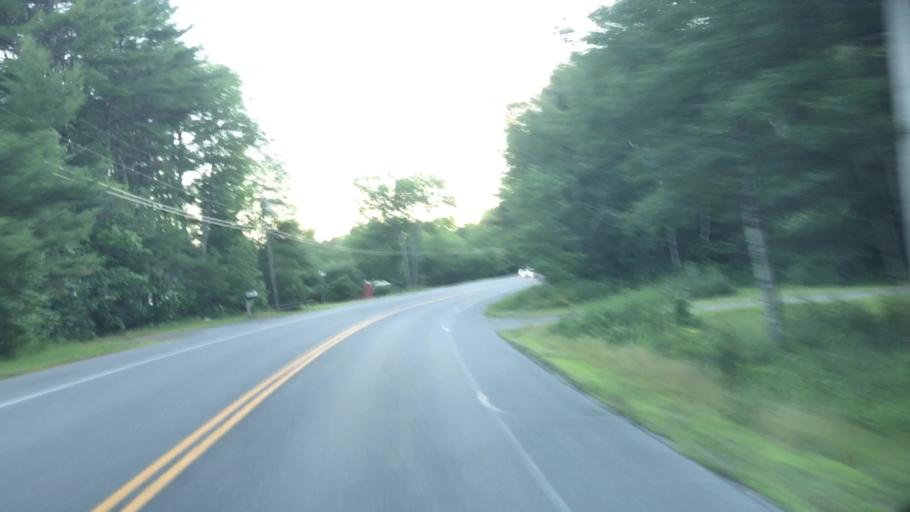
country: US
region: Maine
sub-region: Penobscot County
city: Lincoln
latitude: 45.3739
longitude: -68.4714
